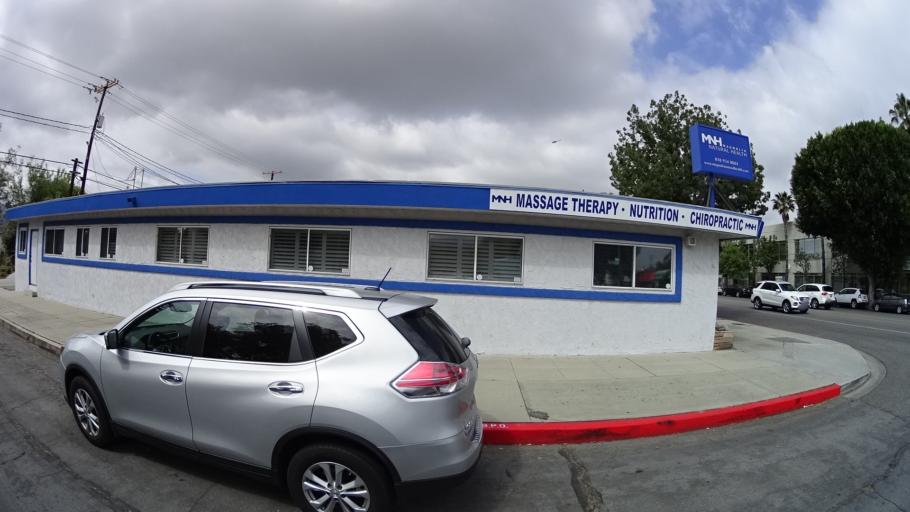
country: US
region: California
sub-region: Los Angeles County
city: Burbank
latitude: 34.1728
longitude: -118.3316
